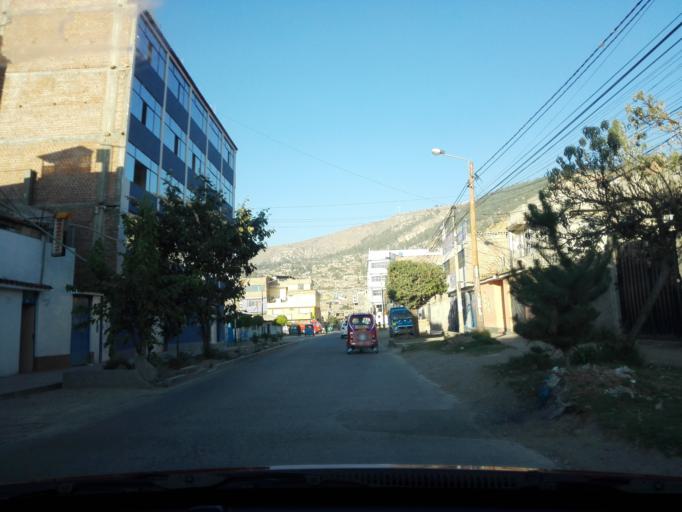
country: PE
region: Ayacucho
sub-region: Provincia de Huamanga
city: Ayacucho
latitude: -13.1480
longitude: -74.2269
